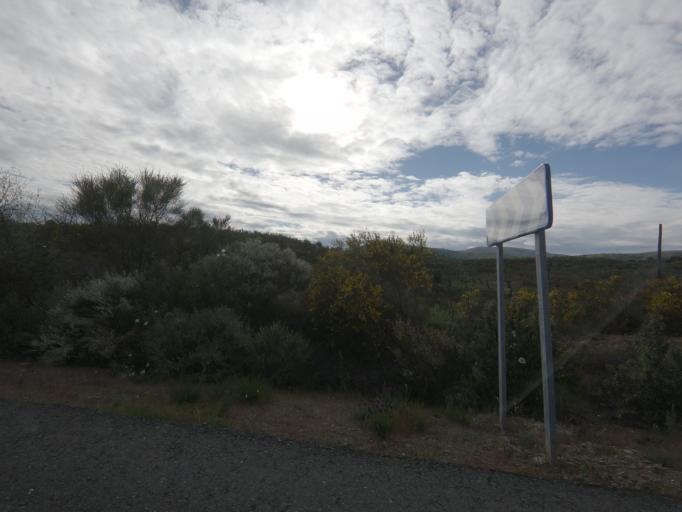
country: ES
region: Extremadura
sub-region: Provincia de Caceres
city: Perales del Puerto
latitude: 40.1325
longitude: -6.6796
